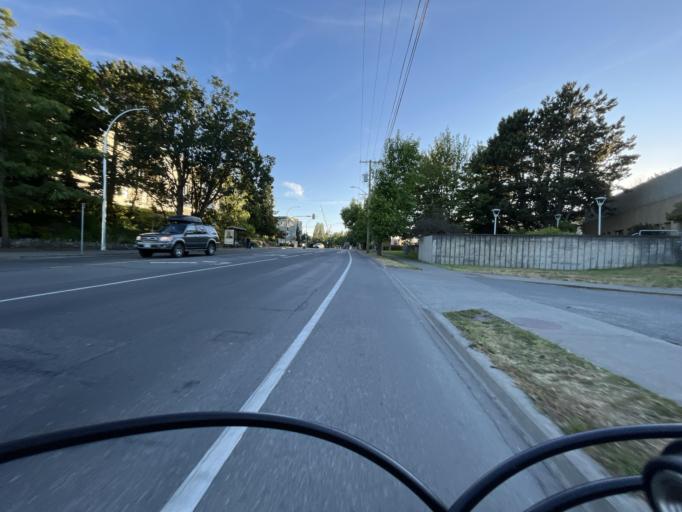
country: CA
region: British Columbia
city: Oak Bay
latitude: 48.4318
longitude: -123.3248
